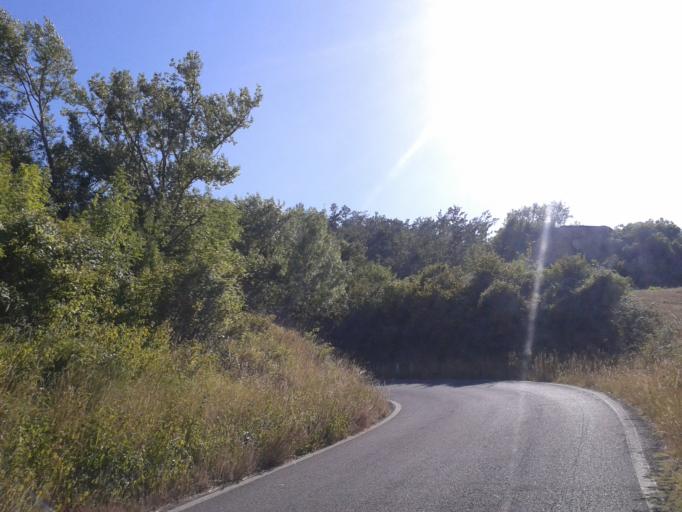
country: IT
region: Tuscany
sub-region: Province of Pisa
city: Chianni
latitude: 43.4553
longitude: 10.6268
